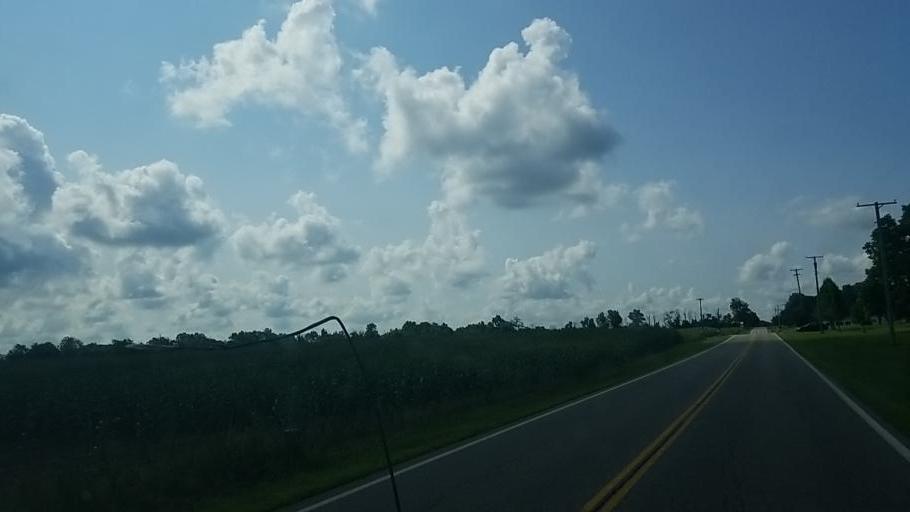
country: US
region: Ohio
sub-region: Ashland County
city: Ashland
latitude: 40.7672
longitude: -82.3068
